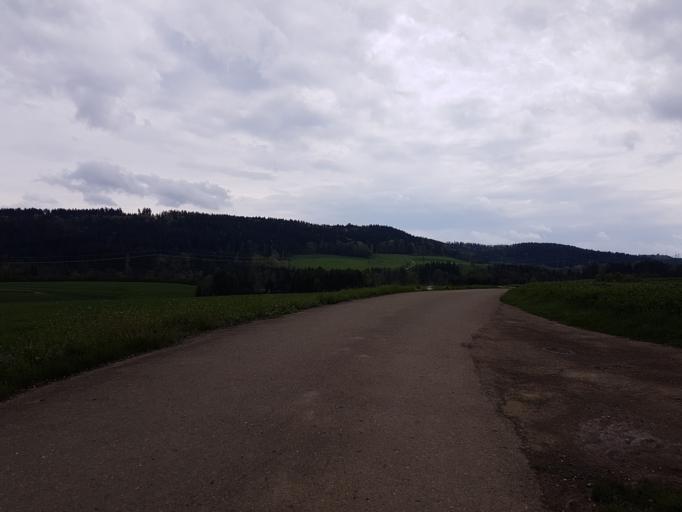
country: CH
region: Schaffhausen
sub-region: Bezirk Schleitheim
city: Schleitheim
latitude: 47.7927
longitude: 8.5087
